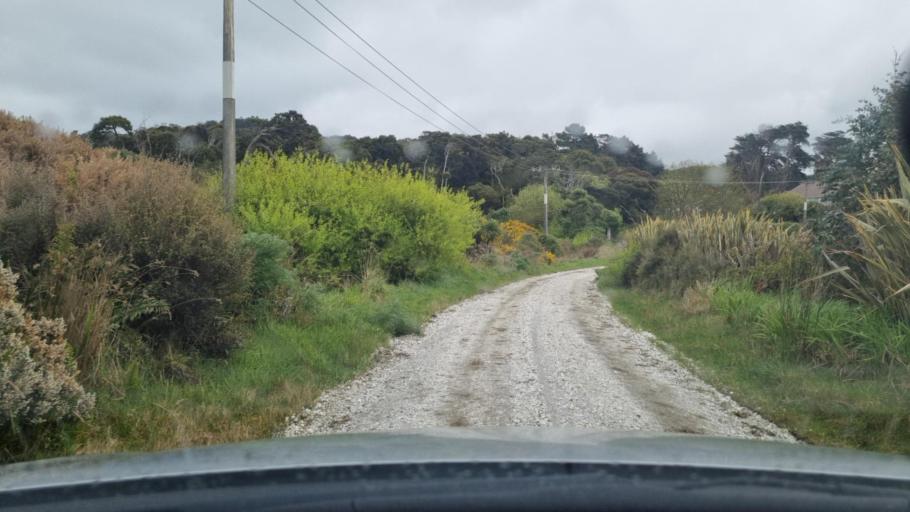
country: NZ
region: Southland
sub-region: Invercargill City
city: Bluff
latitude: -46.5877
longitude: 168.3028
